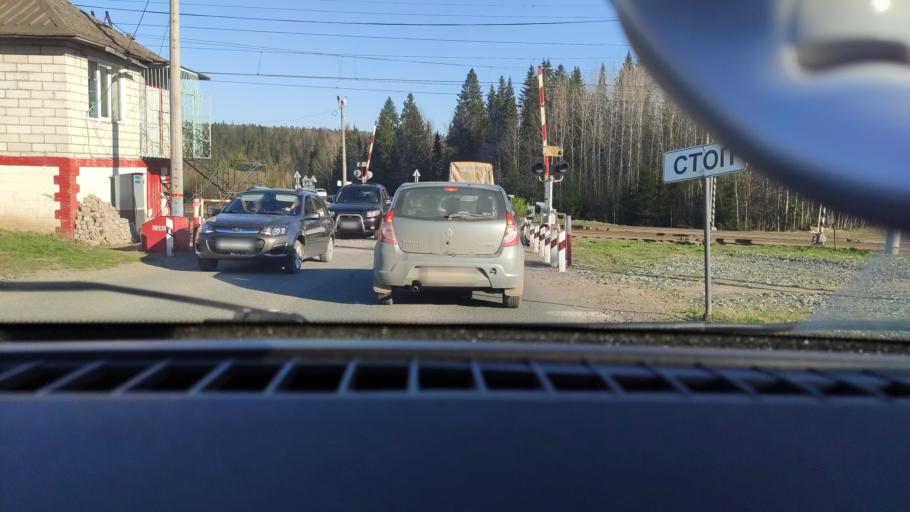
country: RU
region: Perm
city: Polazna
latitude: 58.1220
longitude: 56.4481
